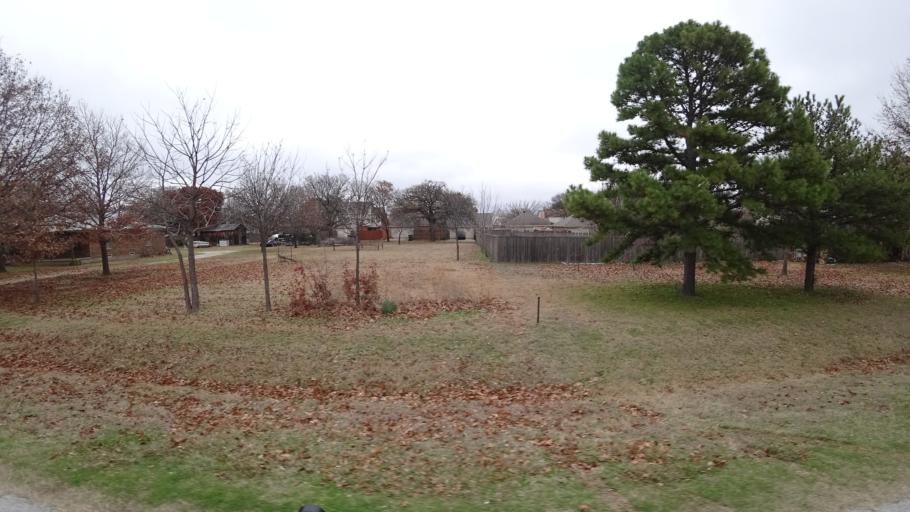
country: US
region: Texas
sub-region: Denton County
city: Lewisville
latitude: 33.0220
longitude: -97.0327
